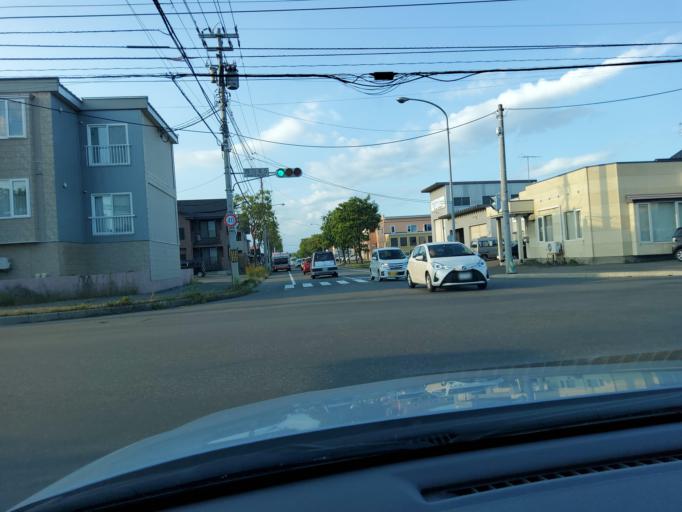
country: JP
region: Hokkaido
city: Obihiro
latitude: 42.9356
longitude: 143.1844
